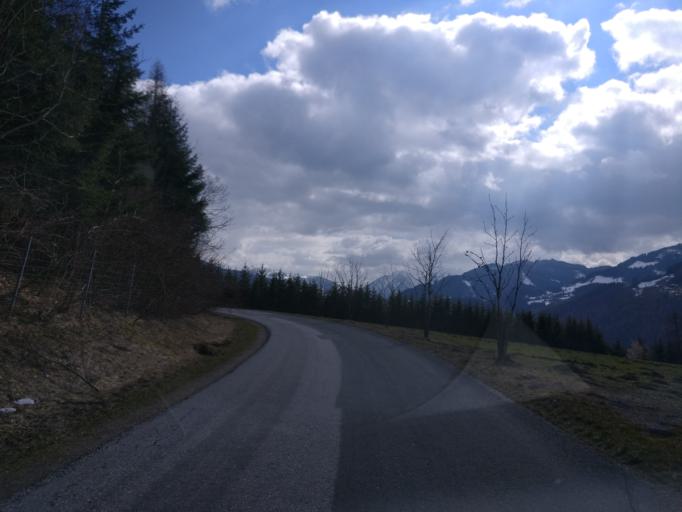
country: AT
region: Salzburg
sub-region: Politischer Bezirk Sankt Johann im Pongau
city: Bischofshofen
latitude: 47.4388
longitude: 13.2209
